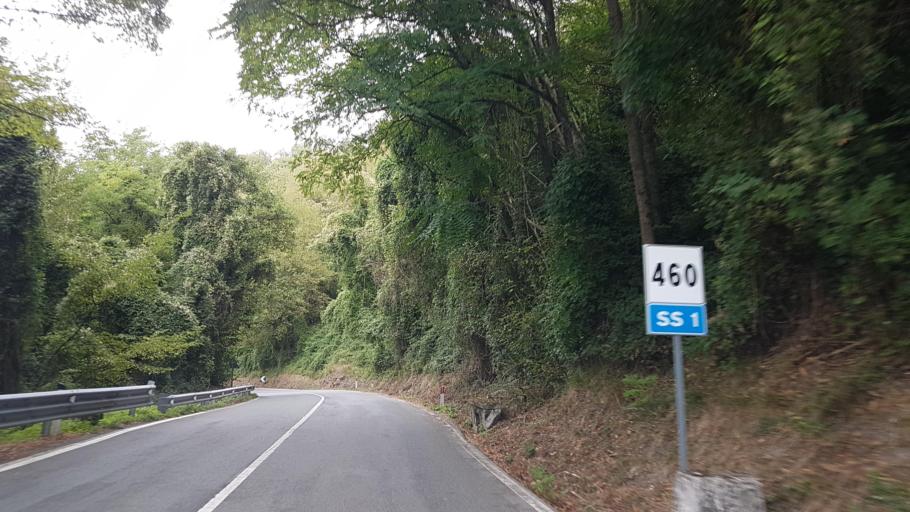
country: IT
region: Liguria
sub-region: Provincia di Genova
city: Castiglione
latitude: 44.2528
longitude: 9.5293
